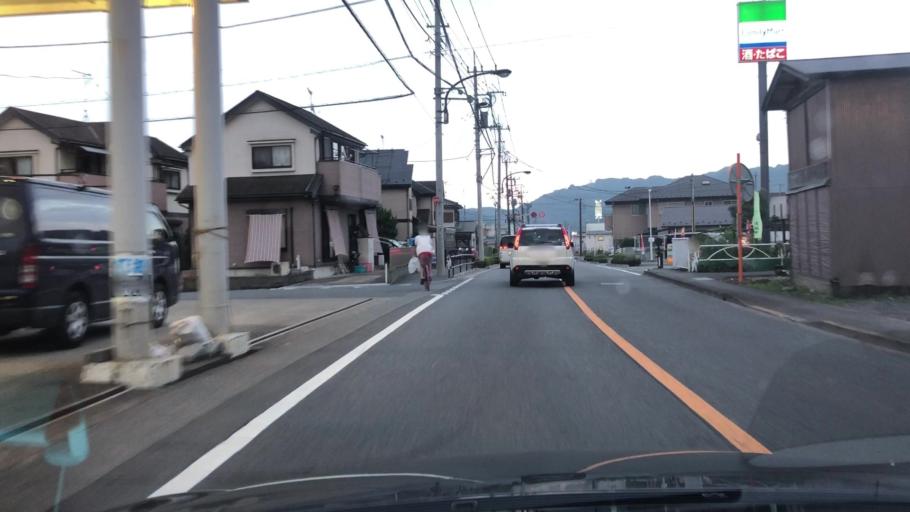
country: JP
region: Tokyo
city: Ome
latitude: 35.7912
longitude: 139.2197
